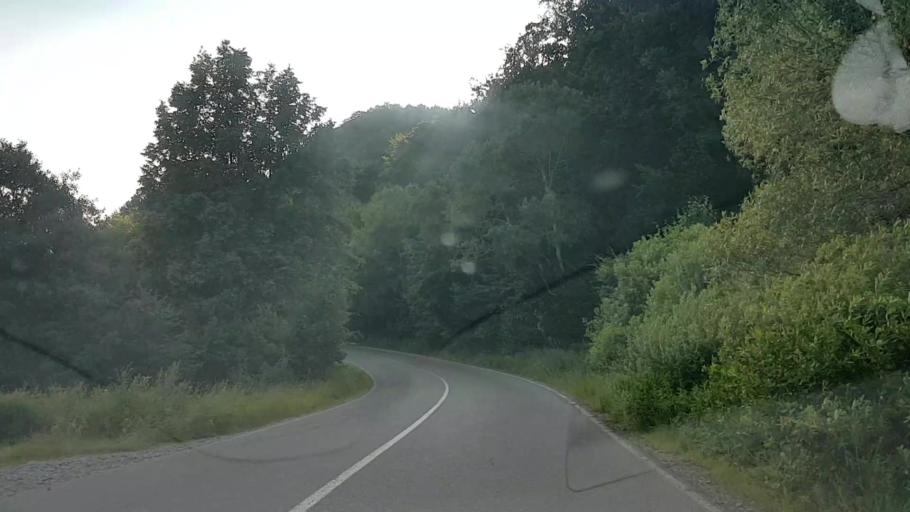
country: RO
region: Harghita
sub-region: Comuna Praid
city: Ocna de Sus
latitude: 46.5719
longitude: 25.1974
